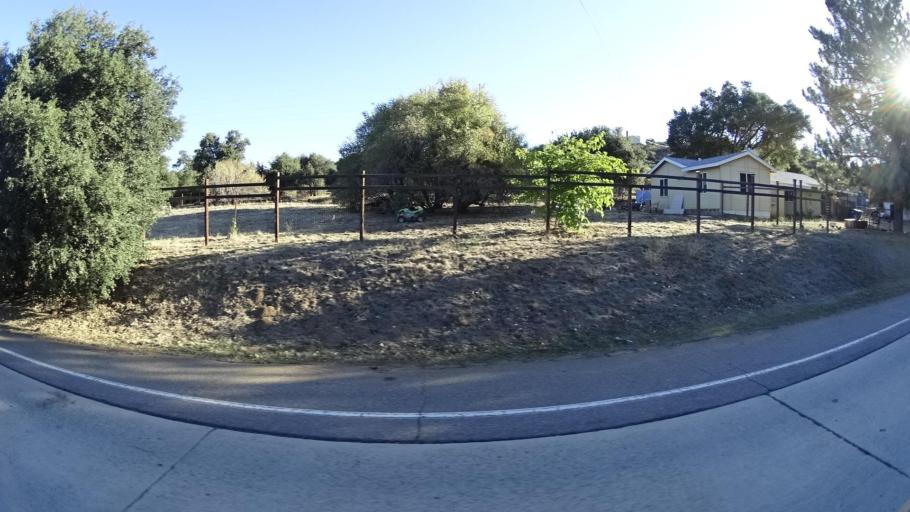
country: US
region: California
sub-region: San Diego County
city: Pine Valley
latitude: 32.8501
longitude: -116.5622
